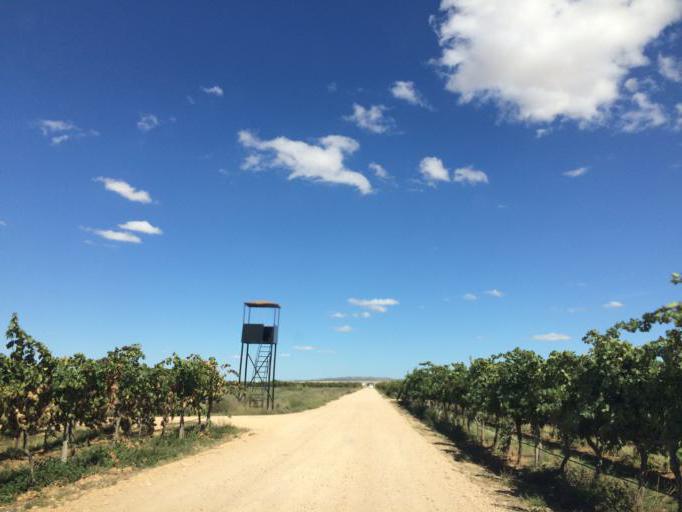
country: ES
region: Castille-La Mancha
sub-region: Provincia de Albacete
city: Albacete
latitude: 38.9321
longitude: -1.8554
